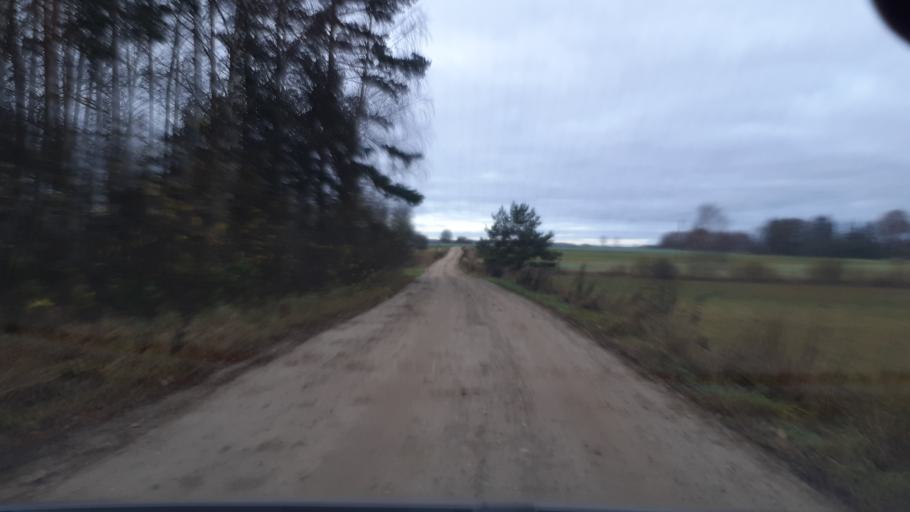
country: LV
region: Kuldigas Rajons
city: Kuldiga
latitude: 56.9984
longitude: 21.9116
